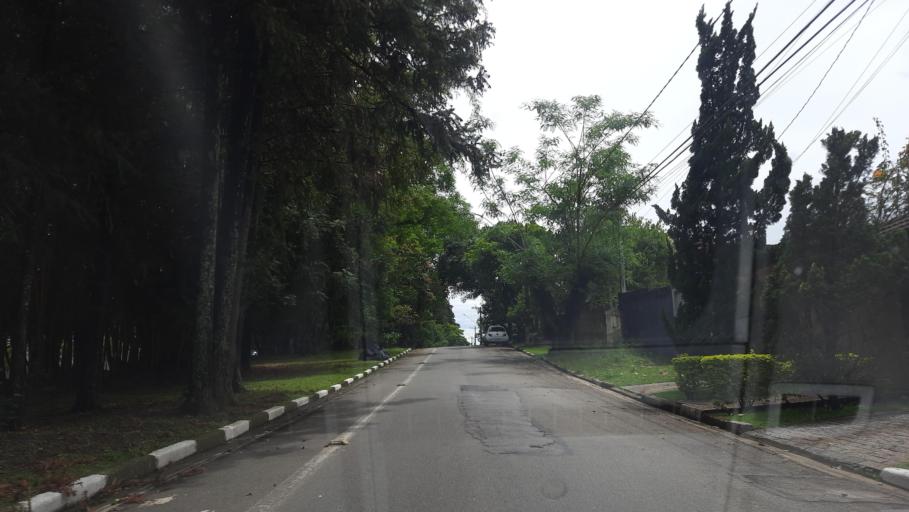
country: BR
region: Sao Paulo
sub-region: Caieiras
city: Caieiras
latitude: -23.3729
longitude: -46.7538
